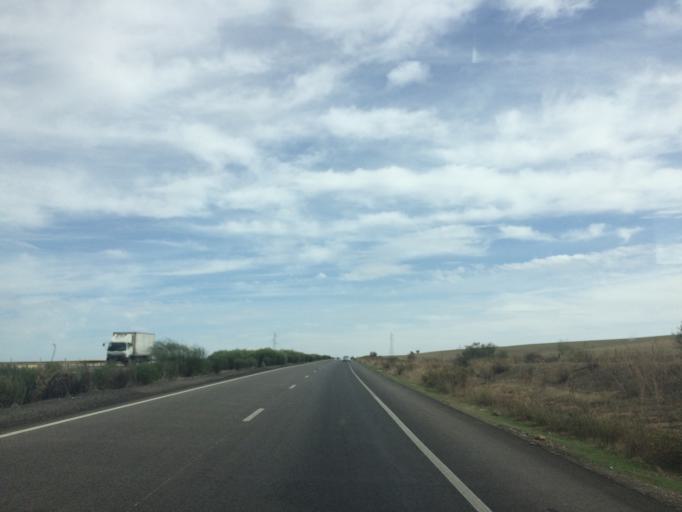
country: MA
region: Meknes-Tafilalet
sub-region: Meknes
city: Meknes
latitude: 33.8745
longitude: -5.7787
